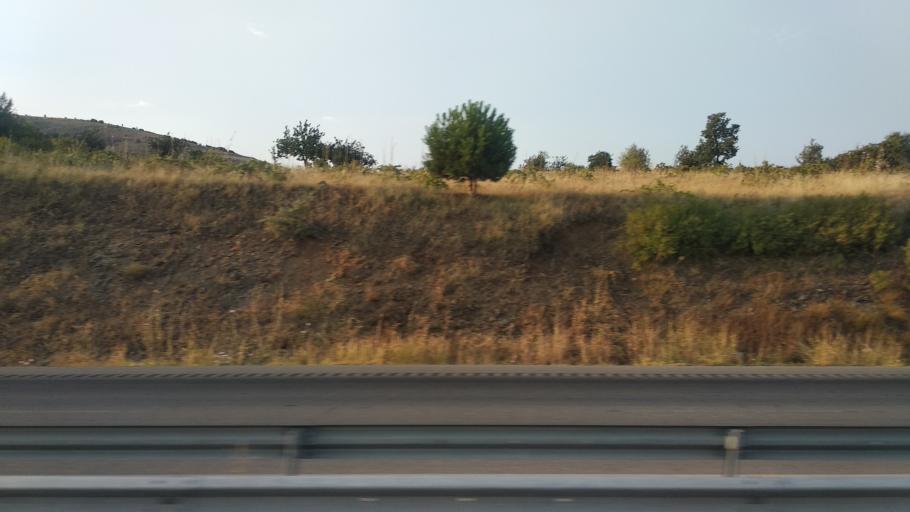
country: TR
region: Manisa
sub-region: Kula
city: Kula
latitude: 38.5678
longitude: 28.5733
